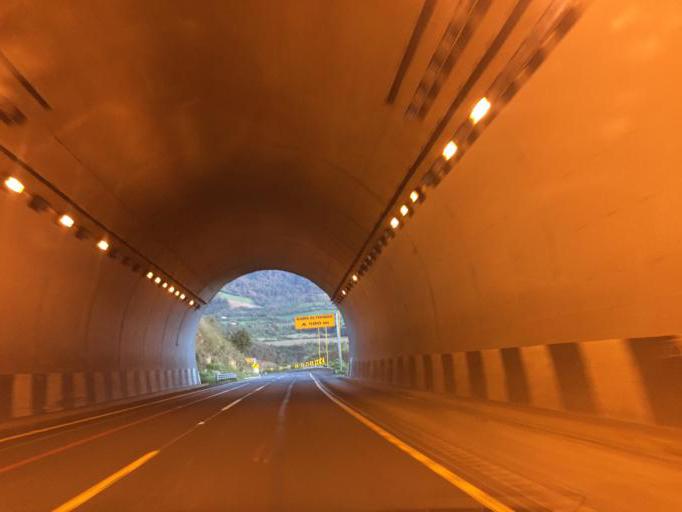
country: MX
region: Puebla
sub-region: Esperanza
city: San Jose Cuyachapa
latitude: 18.8470
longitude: -97.2840
